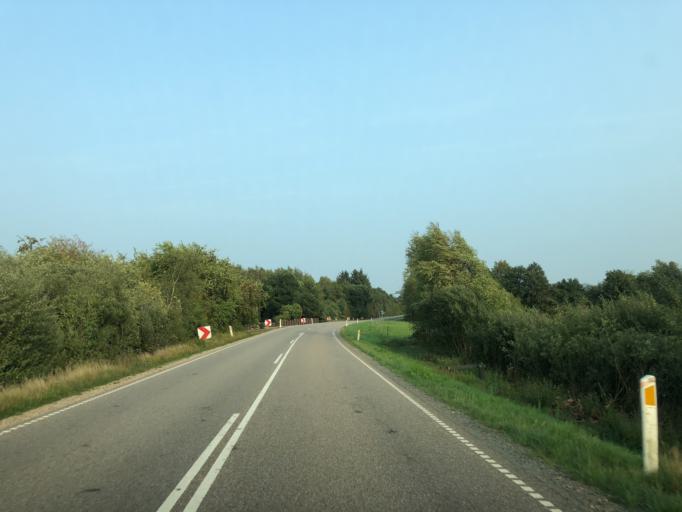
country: DK
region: South Denmark
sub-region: Billund Kommune
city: Grindsted
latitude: 55.8223
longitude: 8.9990
